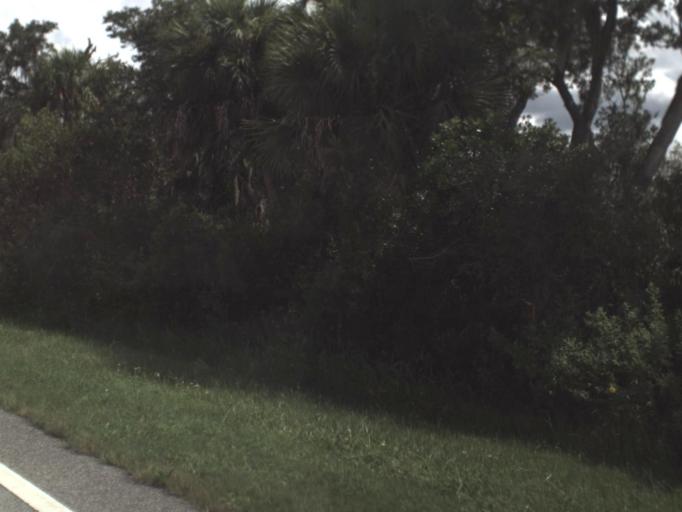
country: US
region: Florida
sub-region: Sarasota County
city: Warm Mineral Springs
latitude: 27.2124
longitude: -82.2612
